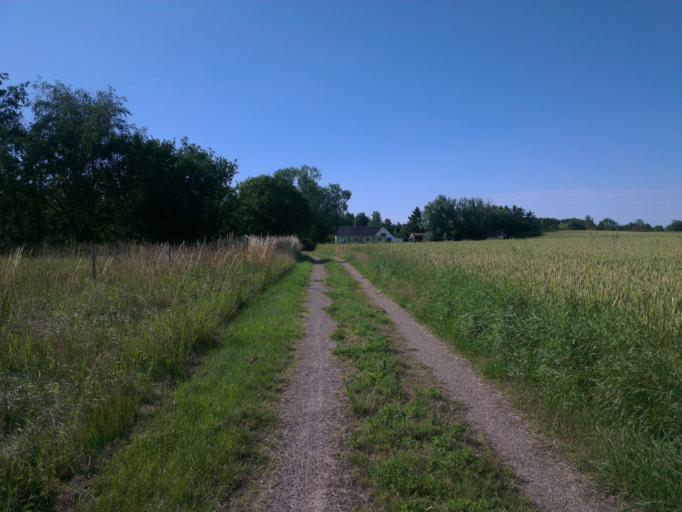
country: DK
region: Capital Region
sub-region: Frederikssund Kommune
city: Frederikssund
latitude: 55.7929
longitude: 12.0422
